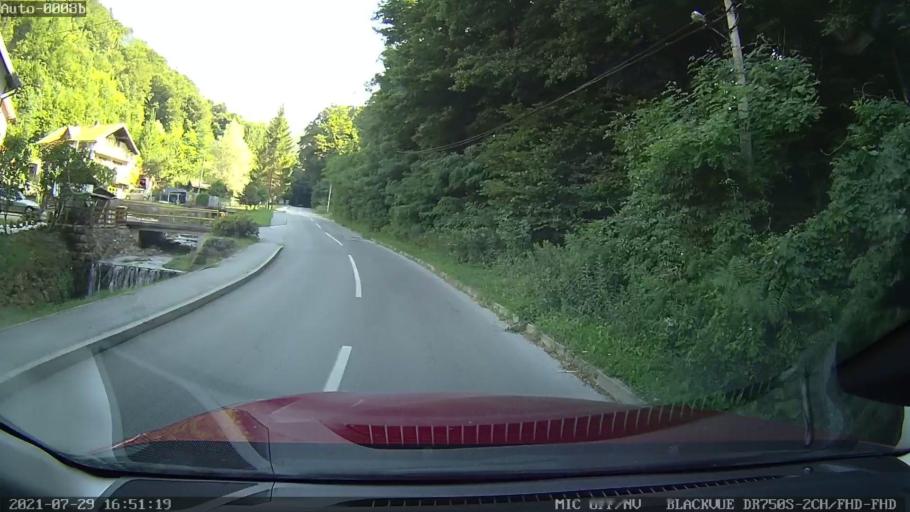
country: HR
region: Varazdinska
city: Ivanec
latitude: 46.2082
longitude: 16.1318
